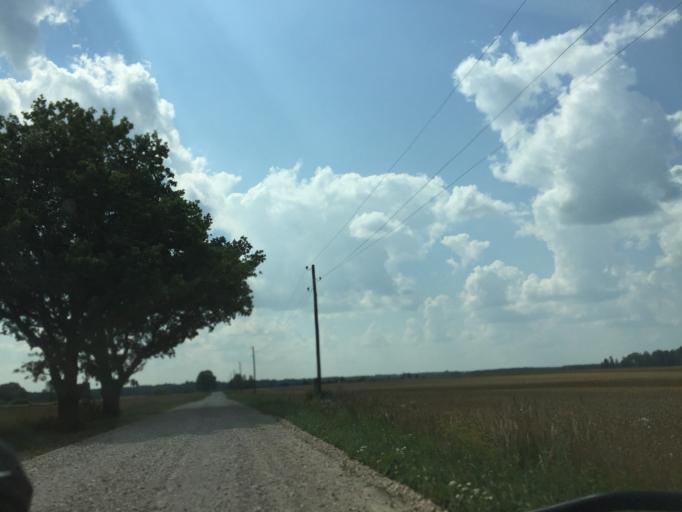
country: LT
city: Zagare
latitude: 56.3862
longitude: 23.1860
